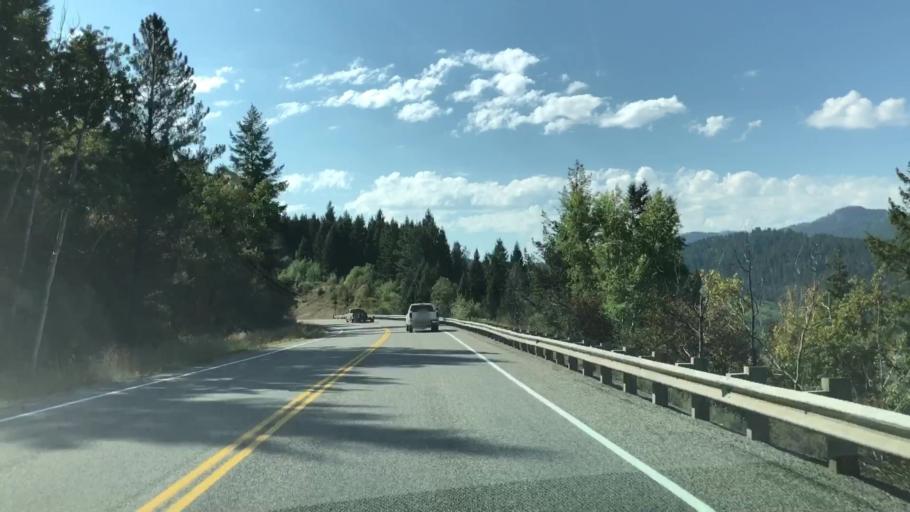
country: US
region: Idaho
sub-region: Teton County
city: Victor
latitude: 43.3210
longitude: -111.1659
